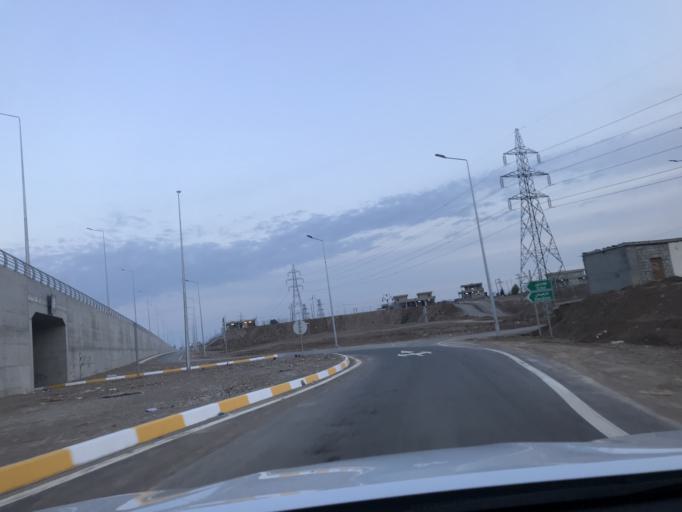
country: IQ
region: Arbil
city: Erbil
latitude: 36.3142
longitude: 43.9112
